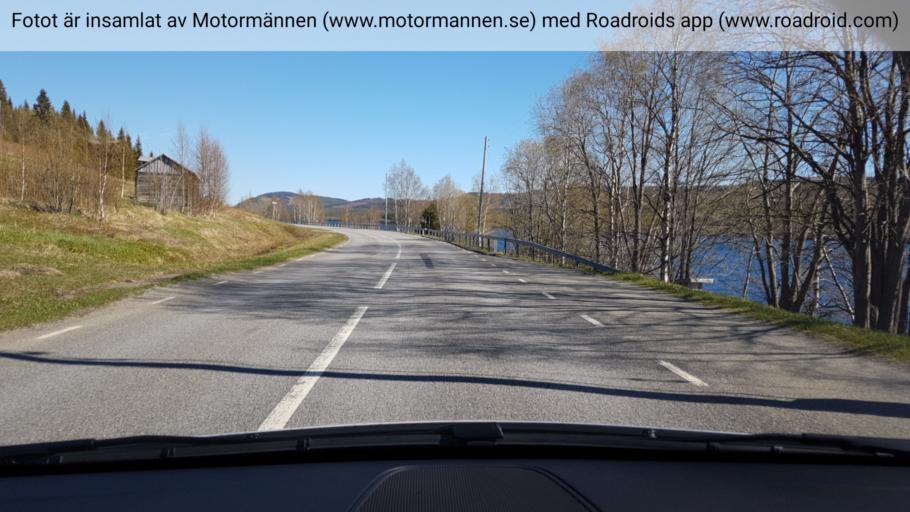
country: NO
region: Nord-Trondelag
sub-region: Lierne
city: Sandvika
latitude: 64.3858
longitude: 14.5330
